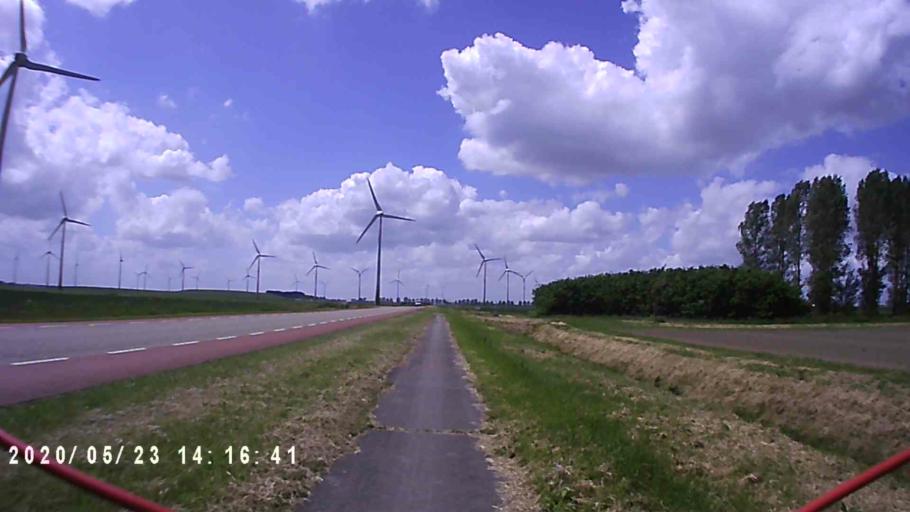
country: NL
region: Groningen
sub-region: Gemeente Delfzijl
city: Delfzijl
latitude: 53.2873
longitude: 6.9971
